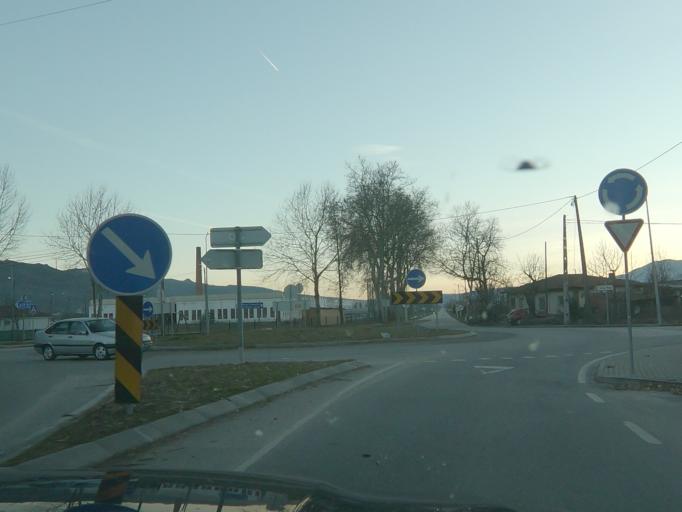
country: PT
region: Vila Real
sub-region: Vila Pouca de Aguiar
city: Vila Pouca de Aguiar
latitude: 41.4504
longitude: -7.6699
